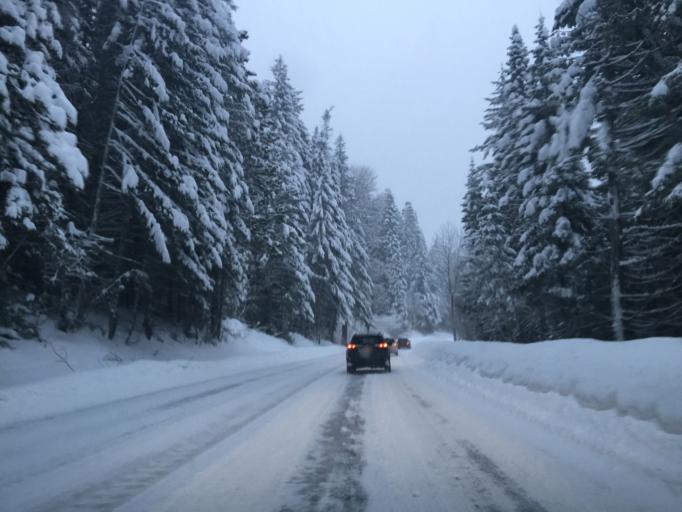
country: US
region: Washington
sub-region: Chelan County
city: Leavenworth
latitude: 47.7835
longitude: -120.9259
